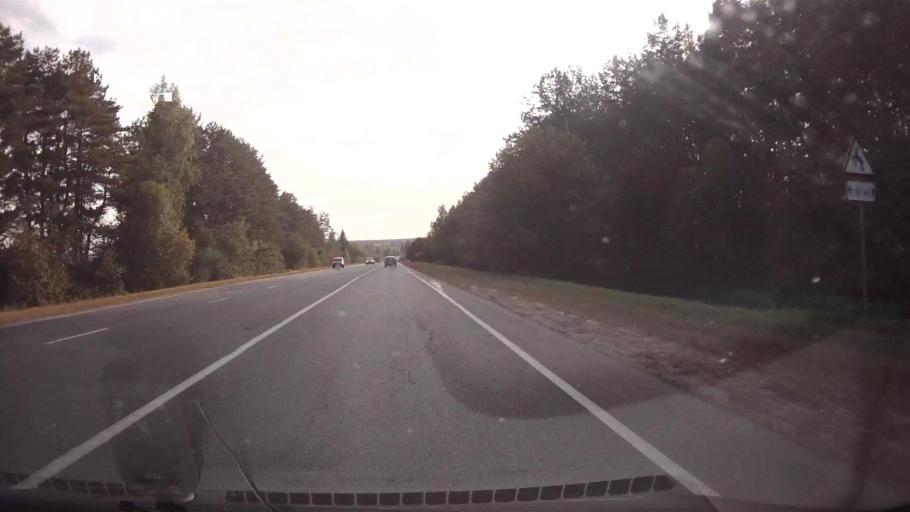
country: RU
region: Mariy-El
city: Sovetskiy
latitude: 56.7809
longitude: 48.6570
